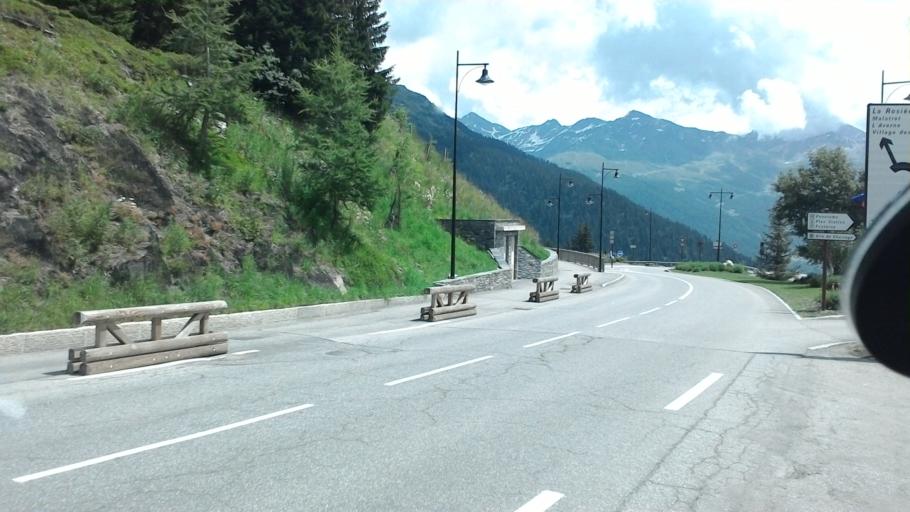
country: FR
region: Rhone-Alpes
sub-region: Departement de la Savoie
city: Seez
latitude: 45.6245
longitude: 6.8572
